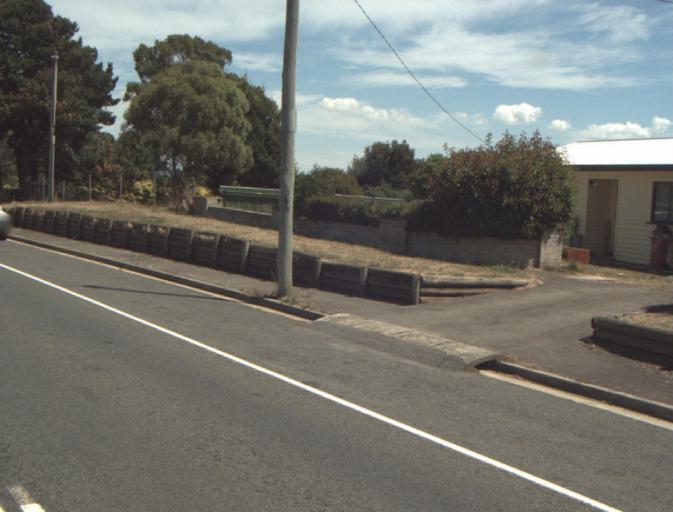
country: AU
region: Tasmania
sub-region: Launceston
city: Mayfield
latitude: -41.3694
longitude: 147.1403
